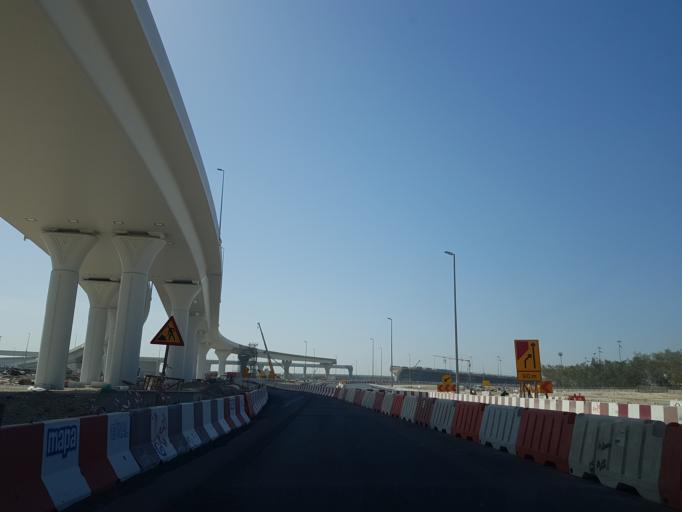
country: AE
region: Dubai
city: Dubai
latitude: 25.0176
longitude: 55.0942
